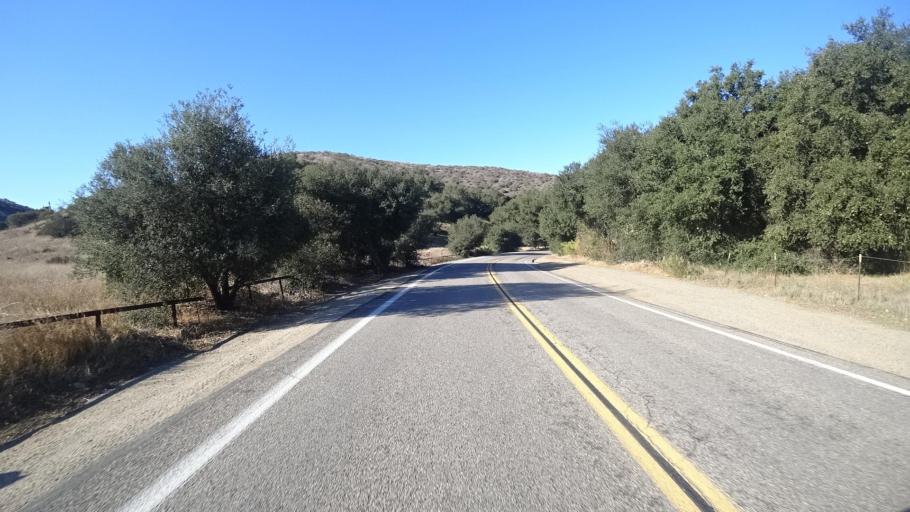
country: US
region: California
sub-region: San Diego County
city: Jamul
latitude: 32.6501
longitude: -116.8628
